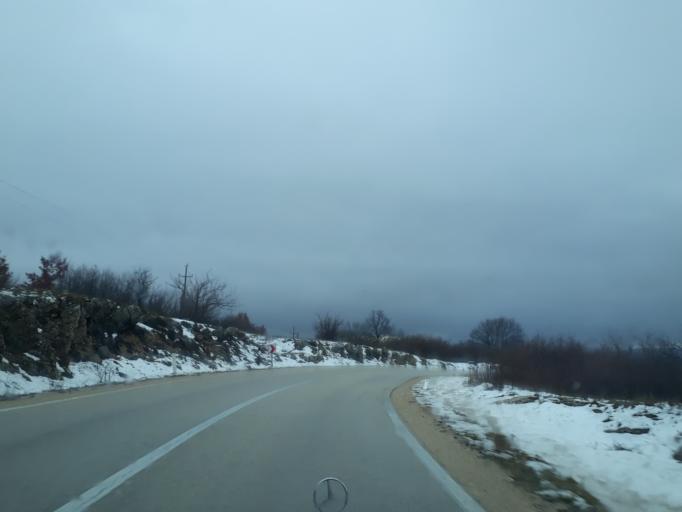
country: BA
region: Federation of Bosnia and Herzegovina
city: Tomislavgrad
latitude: 43.7870
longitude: 17.2230
